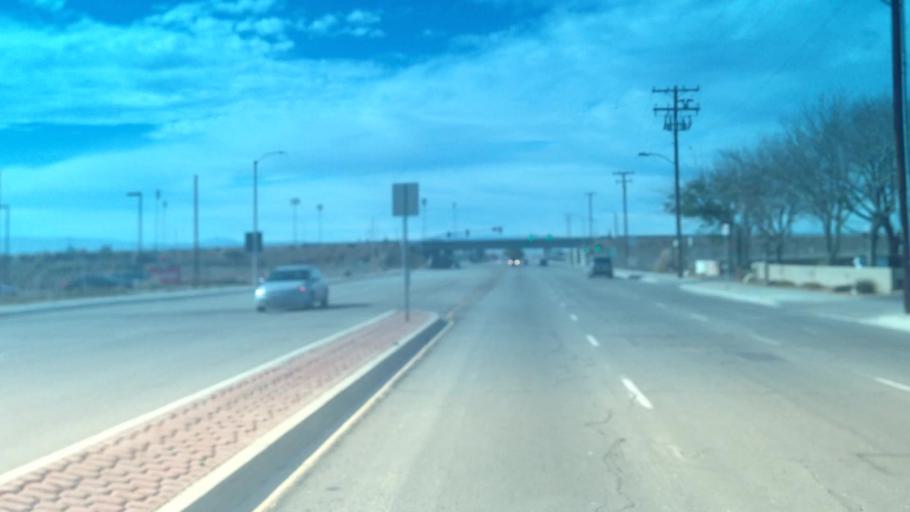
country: US
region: California
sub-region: Los Angeles County
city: Lancaster
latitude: 34.7041
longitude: -118.1670
